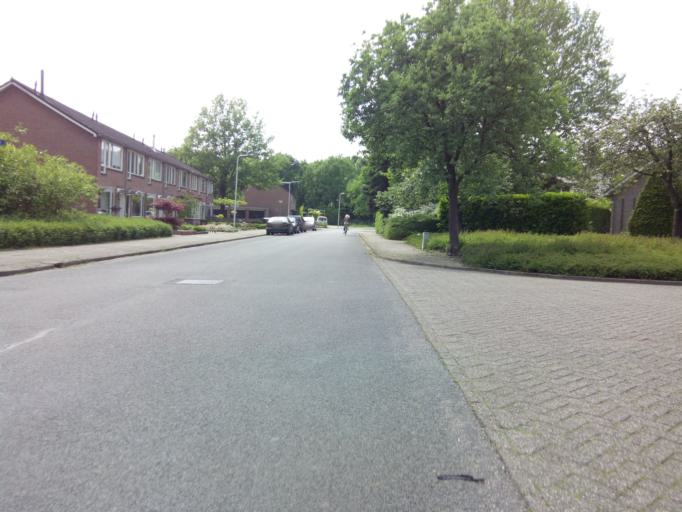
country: NL
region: Gelderland
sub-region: Oost Gelre
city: Lichtenvoorde
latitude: 52.0454
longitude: 6.6032
